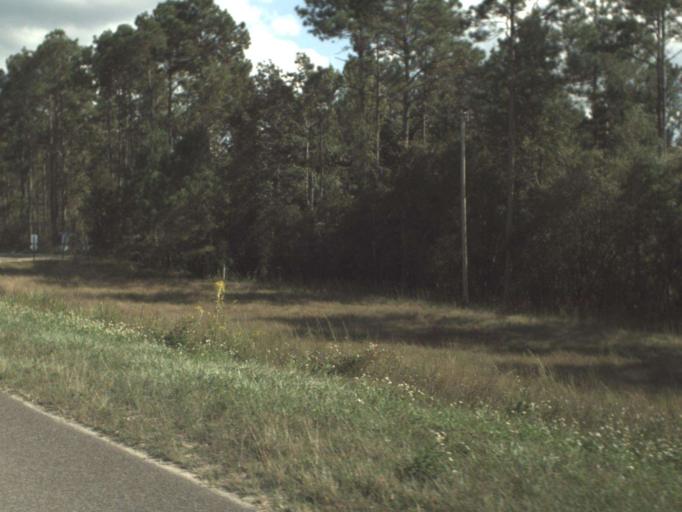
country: US
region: Florida
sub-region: Bay County
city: Laguna Beach
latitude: 30.4527
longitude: -85.9031
